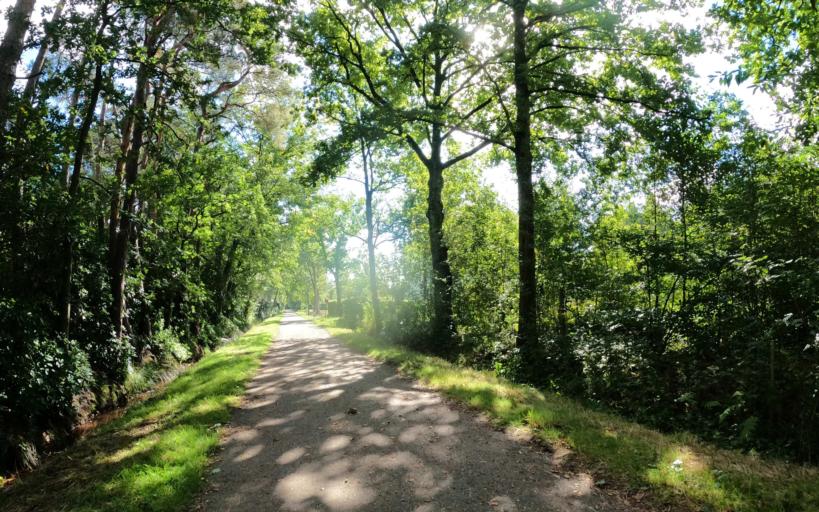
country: BE
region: Flanders
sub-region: Provincie Antwerpen
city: Oostmalle
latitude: 51.2909
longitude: 4.7244
